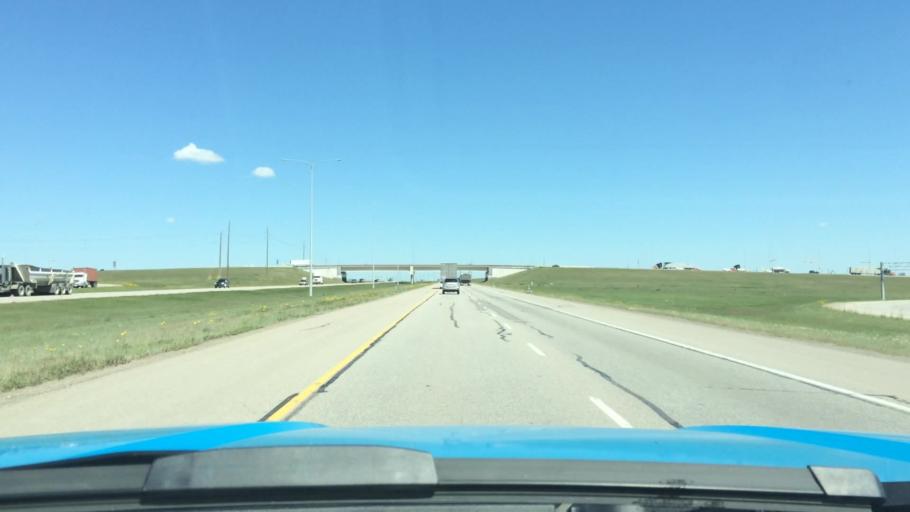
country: CA
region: Alberta
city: Chestermere
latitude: 51.0924
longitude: -113.9186
